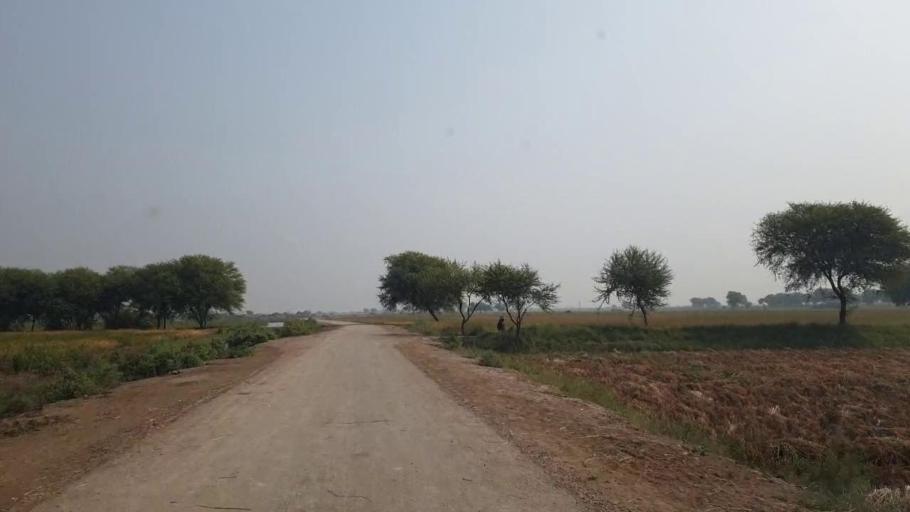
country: PK
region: Sindh
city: Matli
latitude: 25.1308
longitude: 68.7002
